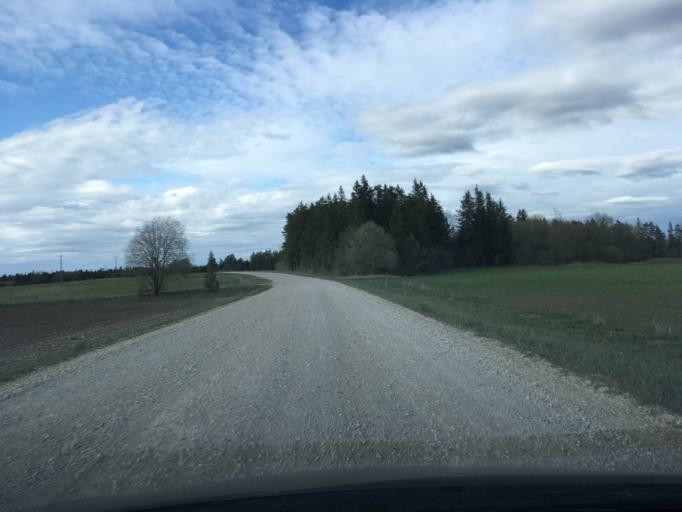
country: EE
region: Raplamaa
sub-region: Maerjamaa vald
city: Marjamaa
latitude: 58.9445
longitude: 24.3172
